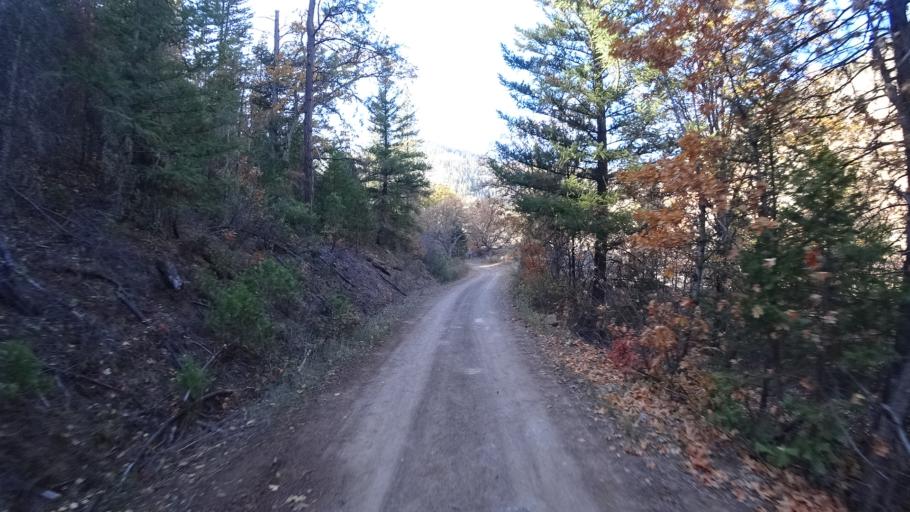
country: US
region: California
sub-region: Siskiyou County
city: Yreka
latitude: 41.8550
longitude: -122.7630
